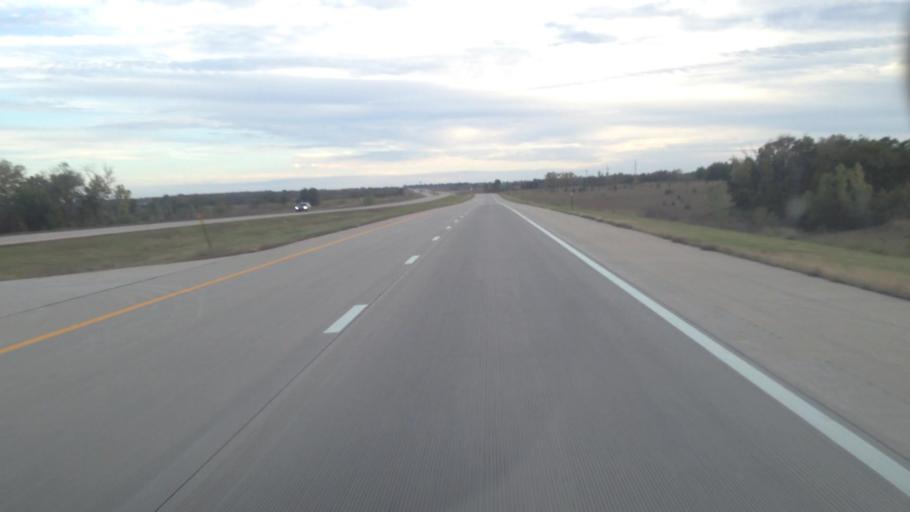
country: US
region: Kansas
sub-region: Douglas County
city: Baldwin City
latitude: 38.7366
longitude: -95.2679
